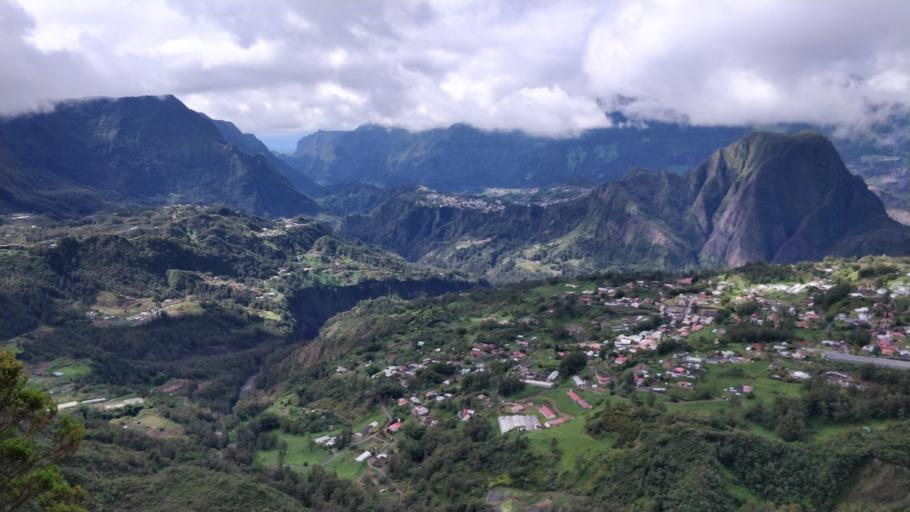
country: RE
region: Reunion
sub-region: Reunion
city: Salazie
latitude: -21.0249
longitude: 55.4617
